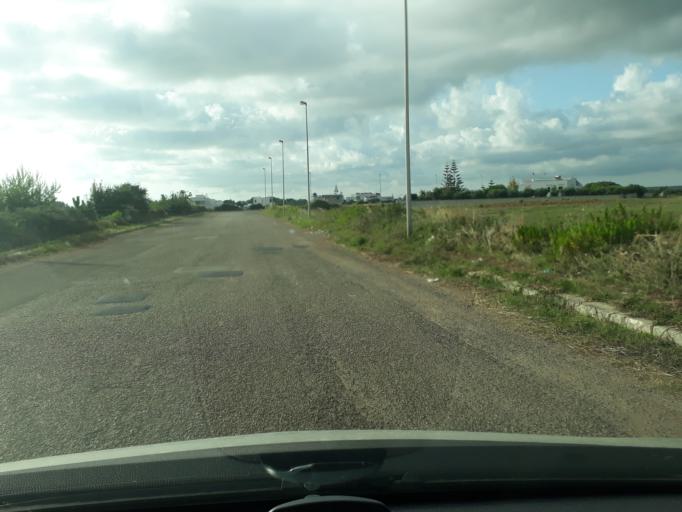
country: IT
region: Apulia
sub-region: Provincia di Brindisi
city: Carovigno
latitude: 40.7610
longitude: 17.6888
